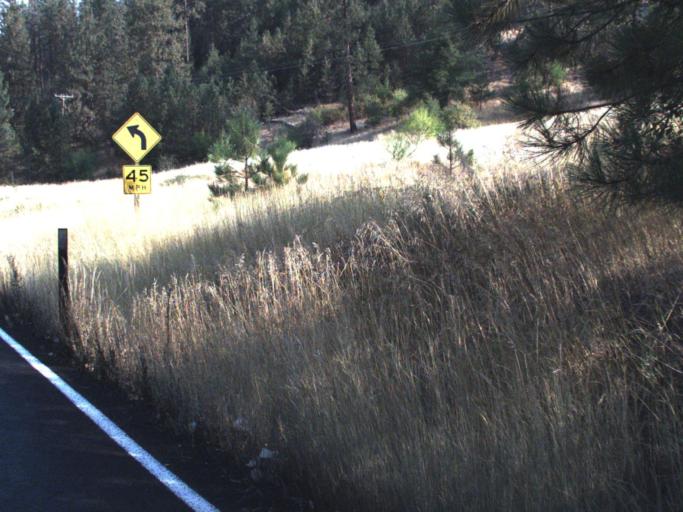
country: US
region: Washington
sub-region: Spokane County
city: Deer Park
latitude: 47.8828
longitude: -117.6575
